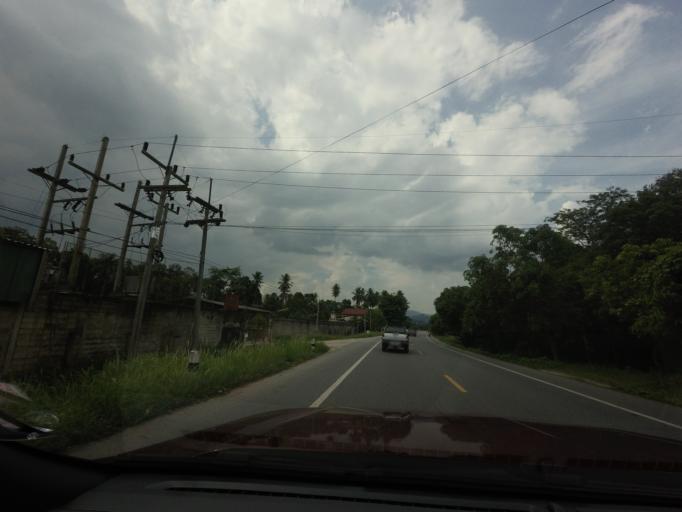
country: TH
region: Yala
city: Ban Nang Sata
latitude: 6.2670
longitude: 101.2783
